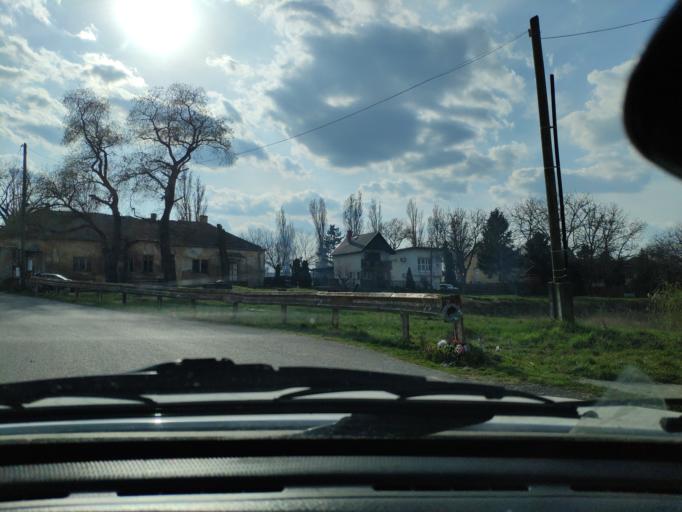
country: HU
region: Fejer
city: Adony
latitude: 47.1134
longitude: 18.8808
